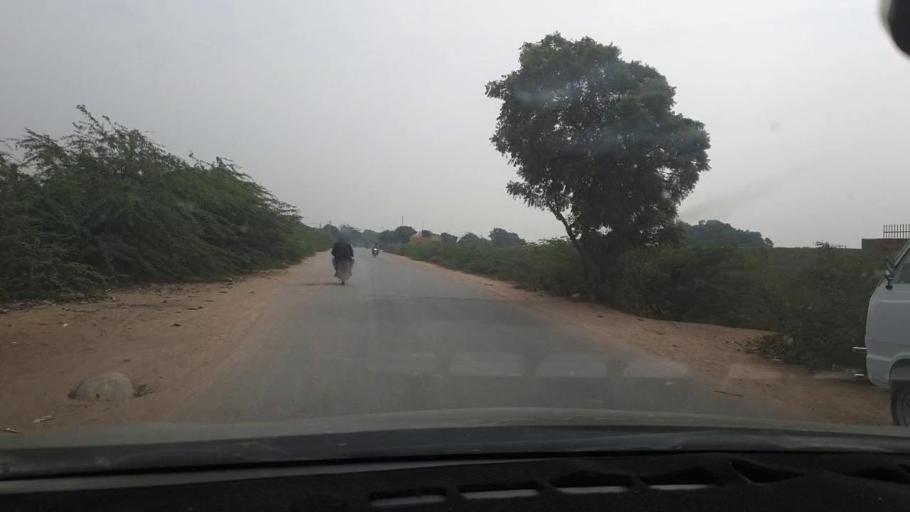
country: PK
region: Sindh
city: Malir Cantonment
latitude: 24.9164
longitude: 67.2601
